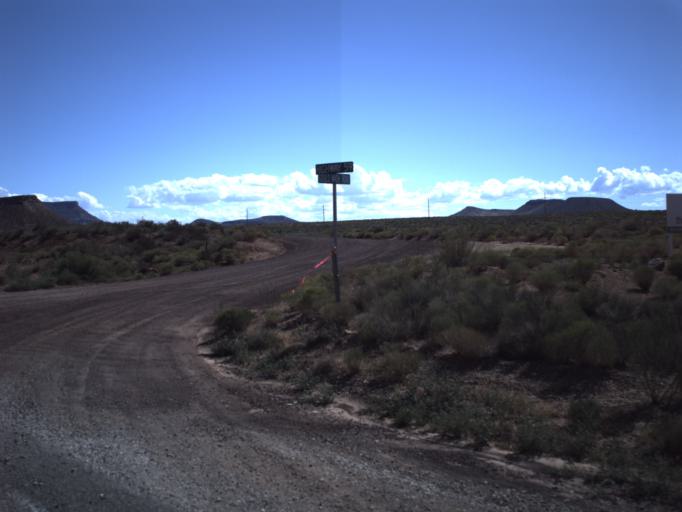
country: US
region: Utah
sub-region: Washington County
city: Hurricane
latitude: 37.1555
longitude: -113.2588
